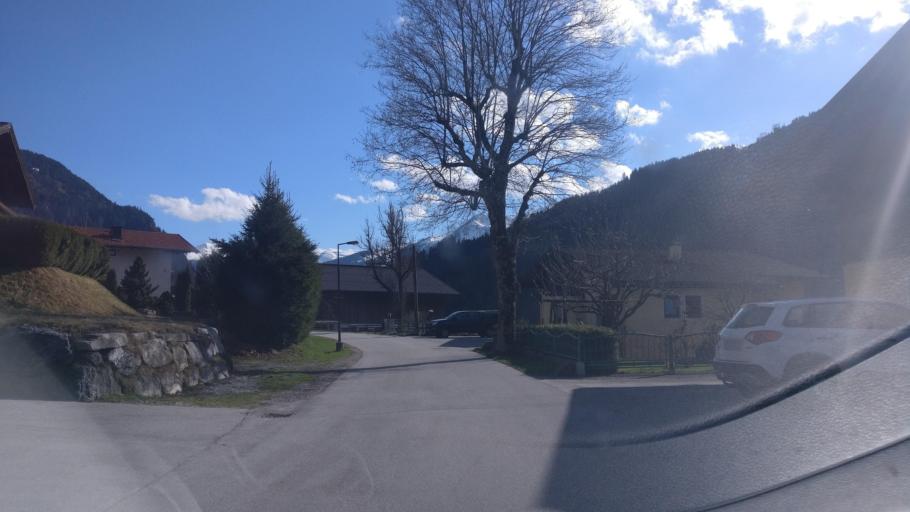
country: AT
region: Salzburg
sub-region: Politischer Bezirk Sankt Johann im Pongau
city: Dorfgastein
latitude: 47.2186
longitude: 13.1103
